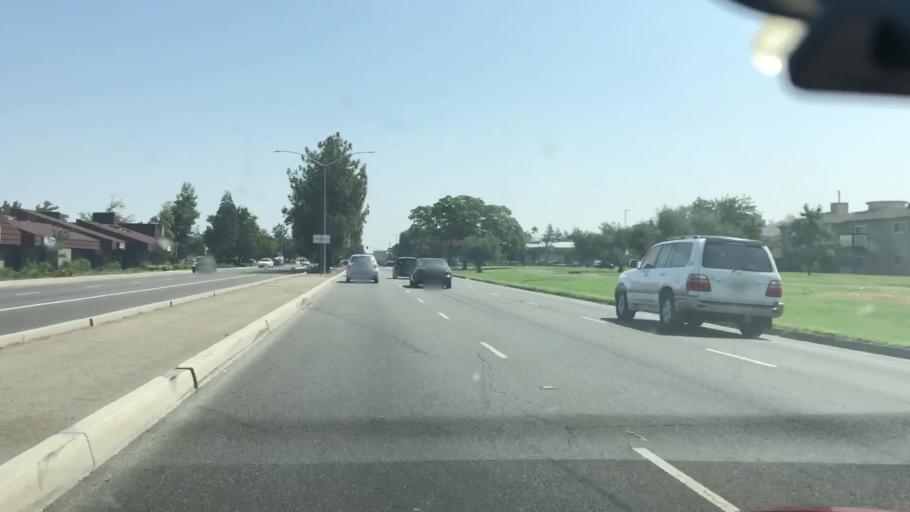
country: US
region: California
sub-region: San Joaquin County
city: Lincoln Village
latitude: 37.9881
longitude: -121.3255
